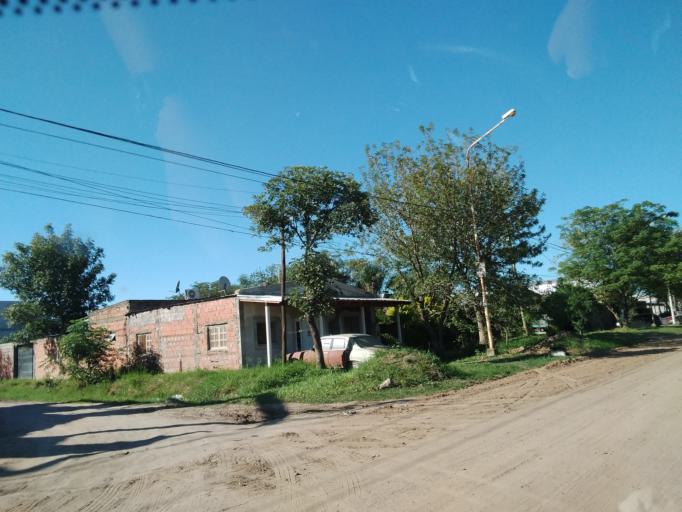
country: AR
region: Corrientes
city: Corrientes
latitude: -27.4600
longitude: -58.7699
